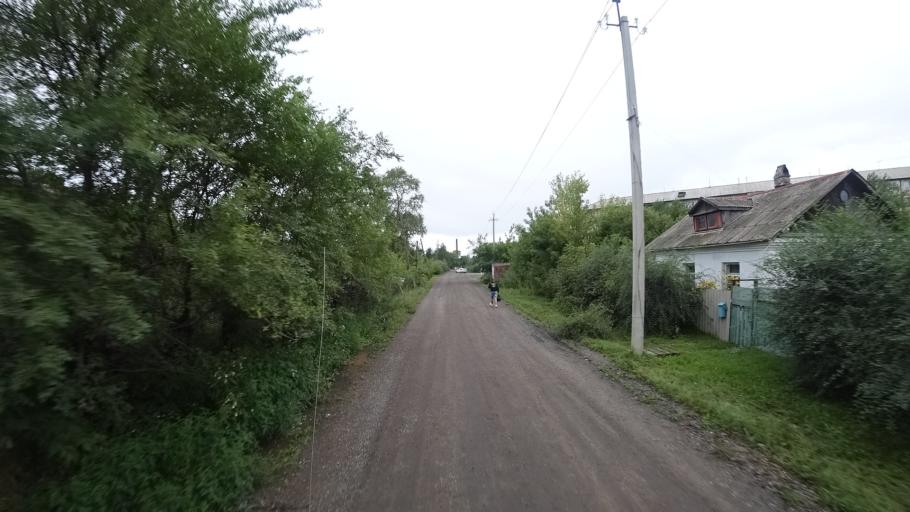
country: RU
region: Primorskiy
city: Chernigovka
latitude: 44.3352
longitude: 132.5329
